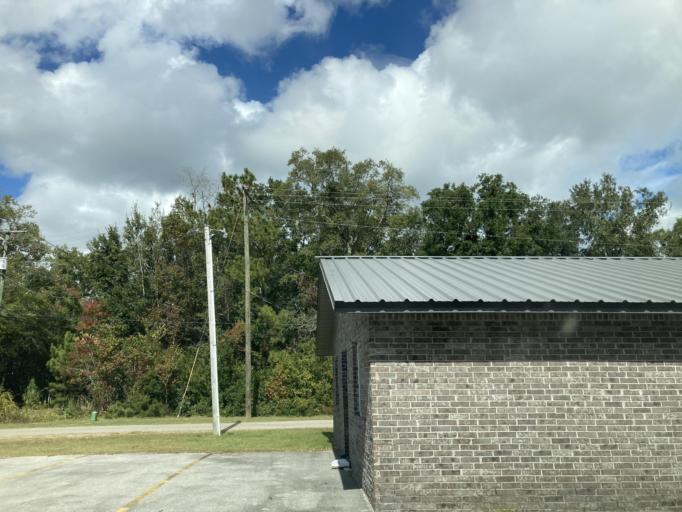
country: US
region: Mississippi
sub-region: Jackson County
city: Gulf Hills
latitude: 30.4481
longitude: -88.8301
